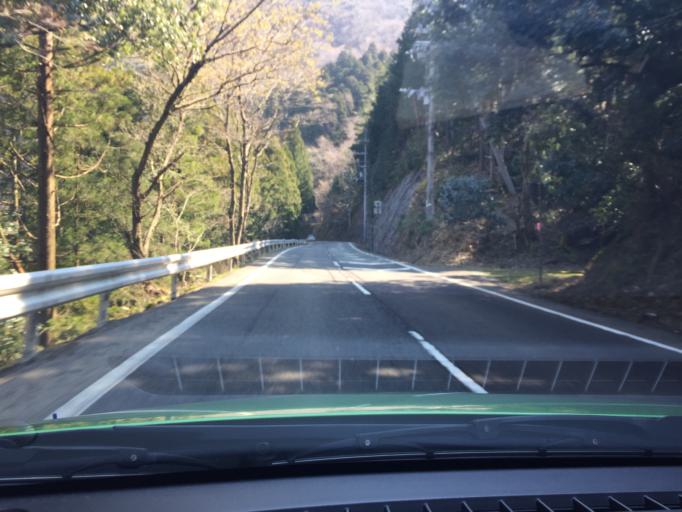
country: JP
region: Fukui
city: Obama
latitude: 35.4281
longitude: 135.6920
